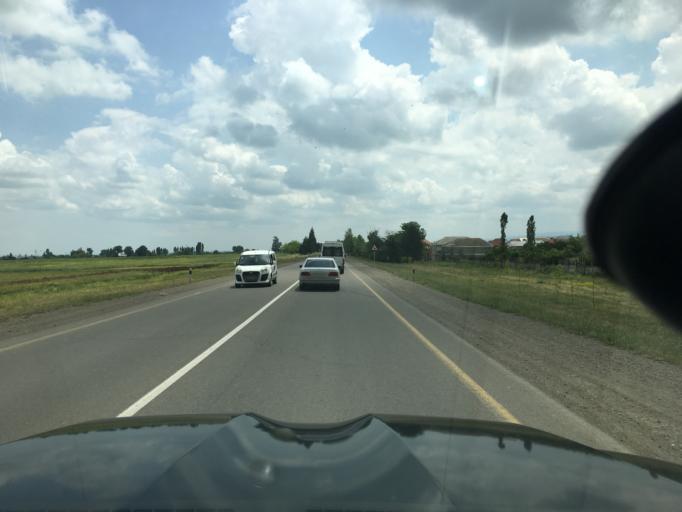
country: AZ
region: Tovuz
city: Tovuz
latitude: 40.9557
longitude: 45.7360
